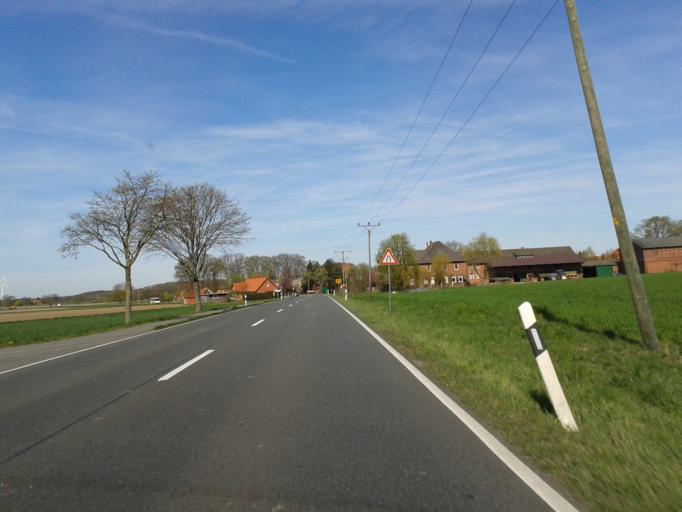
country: DE
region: Lower Saxony
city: Ratzlingen
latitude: 52.9551
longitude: 10.6928
